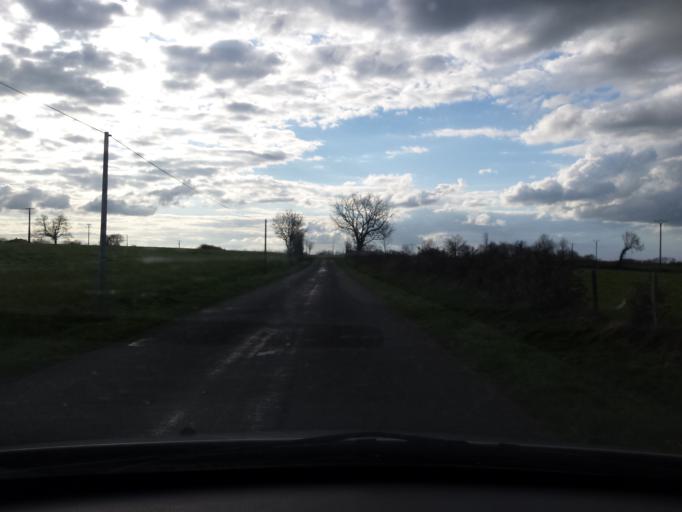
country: FR
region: Pays de la Loire
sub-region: Departement de la Vendee
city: Saint-Martin-des-Noyers
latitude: 46.7222
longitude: -1.1476
